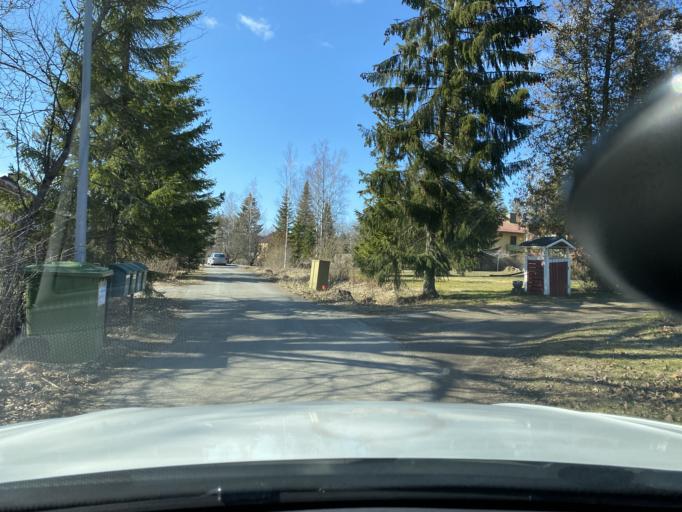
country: FI
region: Pirkanmaa
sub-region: Lounais-Pirkanmaa
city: Punkalaidun
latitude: 61.1093
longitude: 23.1281
